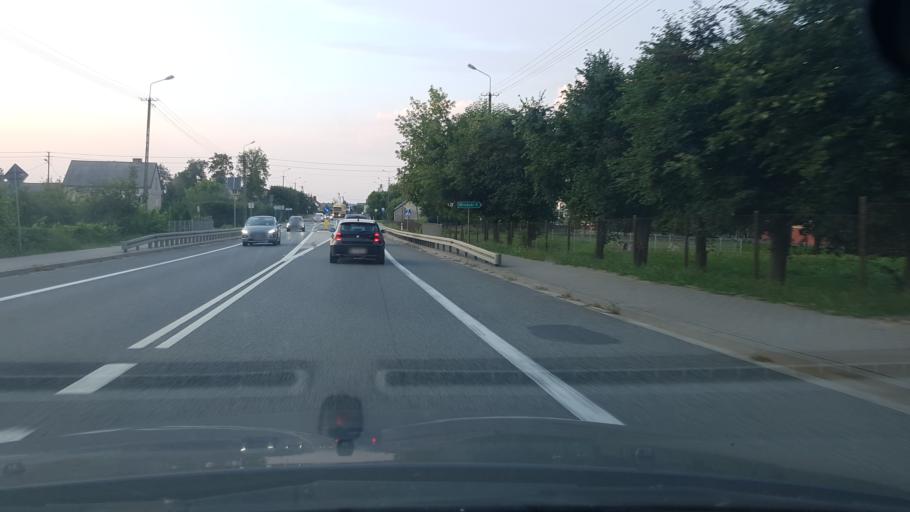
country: PL
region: Masovian Voivodeship
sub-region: Powiat mlawski
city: Mlawa
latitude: 53.1632
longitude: 20.4132
